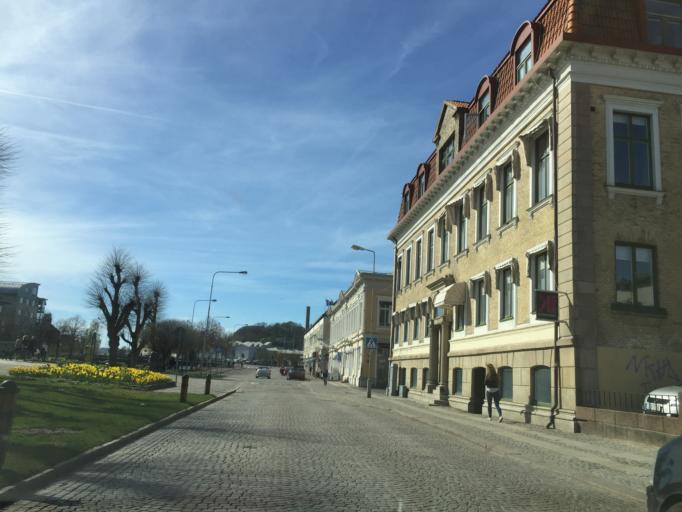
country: SE
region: Vaestra Goetaland
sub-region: Uddevalla Kommun
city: Uddevalla
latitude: 58.3489
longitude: 11.9348
